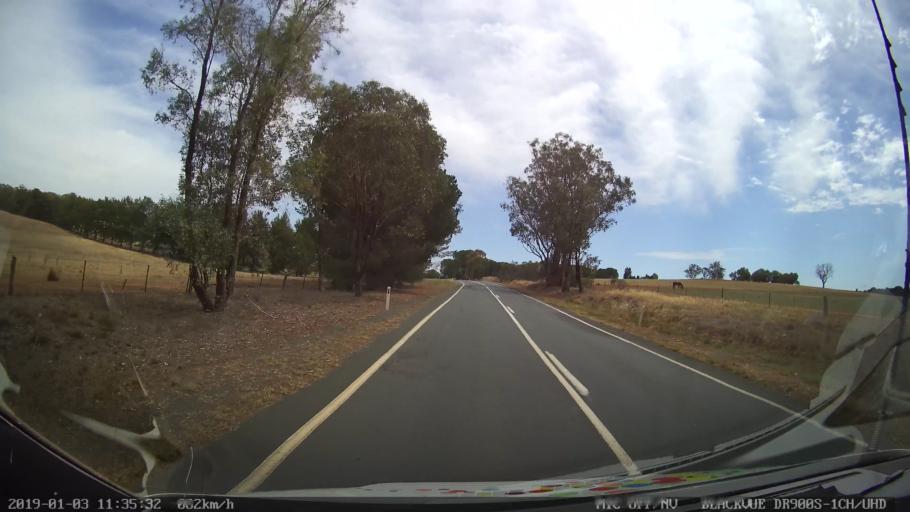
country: AU
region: New South Wales
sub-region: Weddin
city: Grenfell
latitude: -33.9210
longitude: 148.1597
